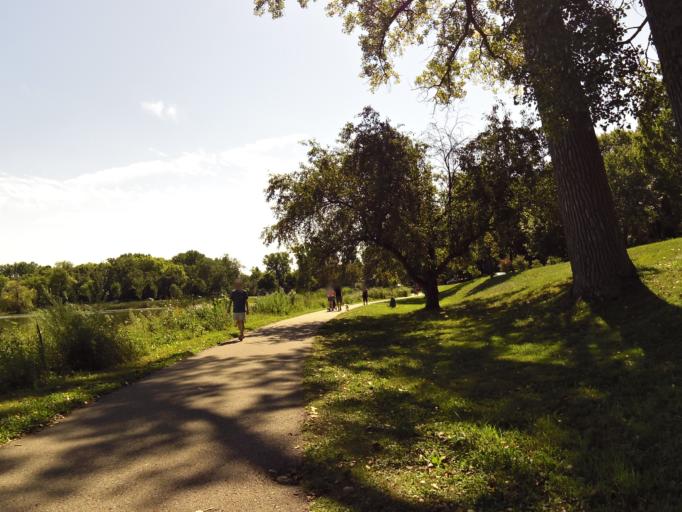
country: US
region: Minnesota
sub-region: Hennepin County
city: Saint Louis Park
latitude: 44.9537
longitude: -93.3116
